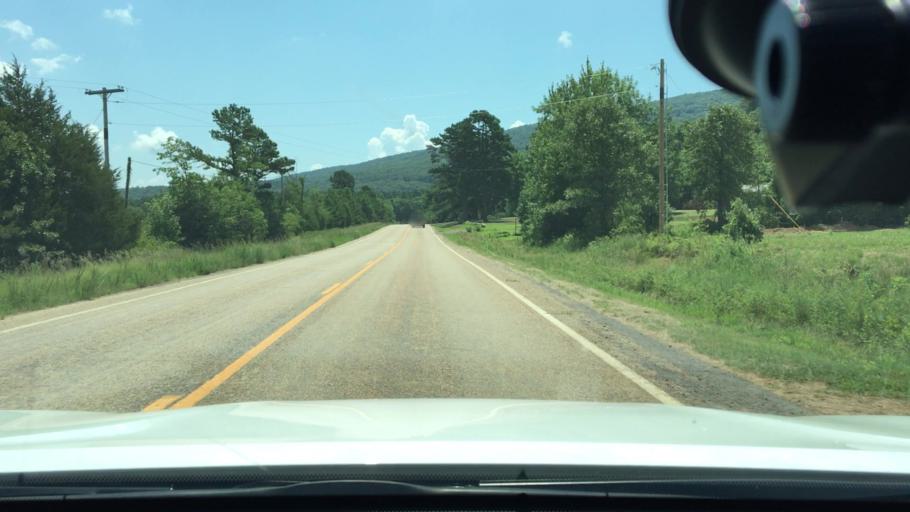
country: US
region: Arkansas
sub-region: Logan County
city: Paris
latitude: 35.1925
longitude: -93.6277
